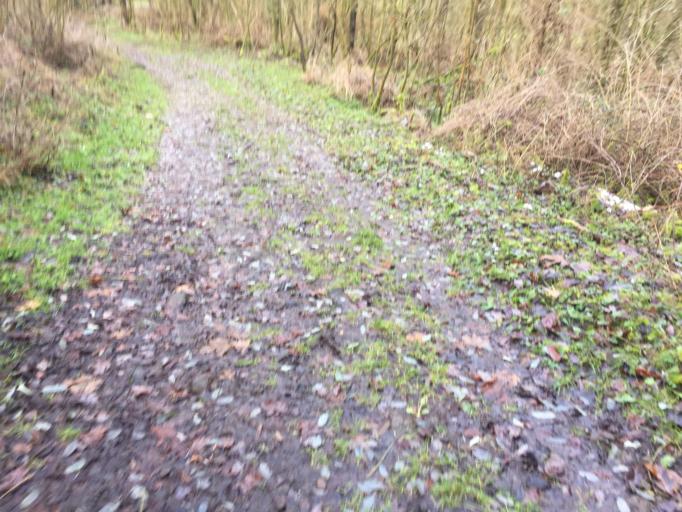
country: DE
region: Hesse
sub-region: Regierungsbezirk Giessen
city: Grunberg
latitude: 50.5894
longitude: 8.9747
